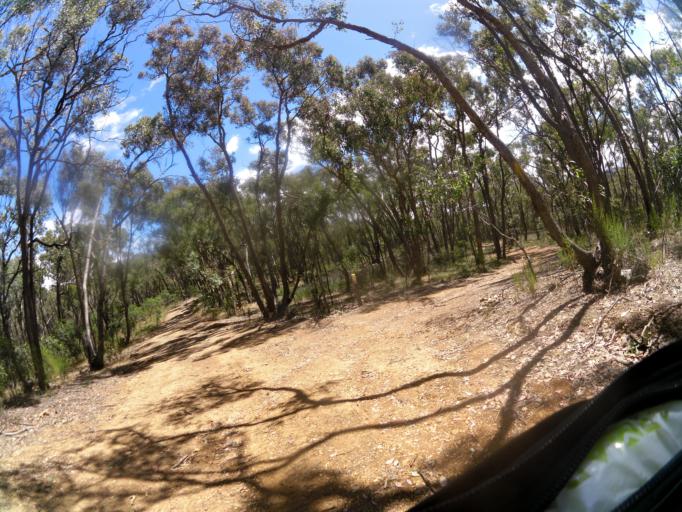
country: AU
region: Victoria
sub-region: Mount Alexander
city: Castlemaine
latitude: -37.0649
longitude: 144.2660
